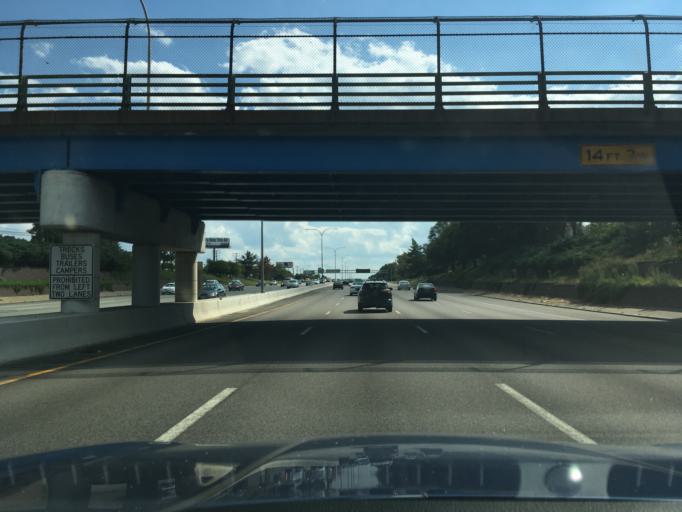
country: US
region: Rhode Island
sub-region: Providence County
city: Cranston
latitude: 41.7732
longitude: -71.4277
